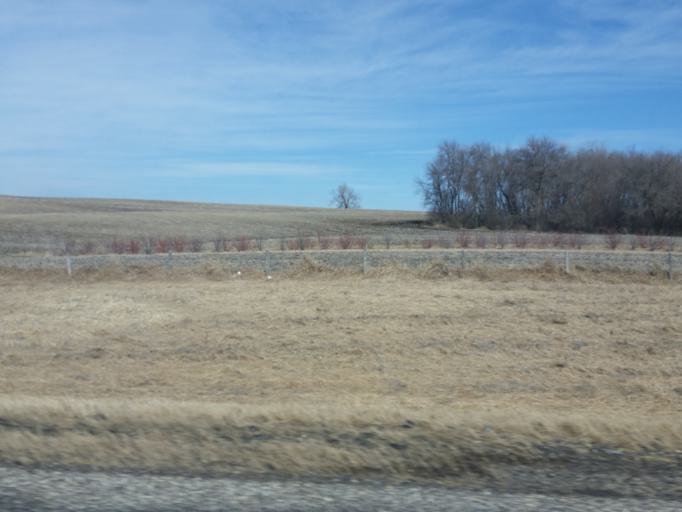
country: US
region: Minnesota
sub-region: Otter Tail County
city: Pelican Rapids
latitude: 46.4294
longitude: -96.2251
